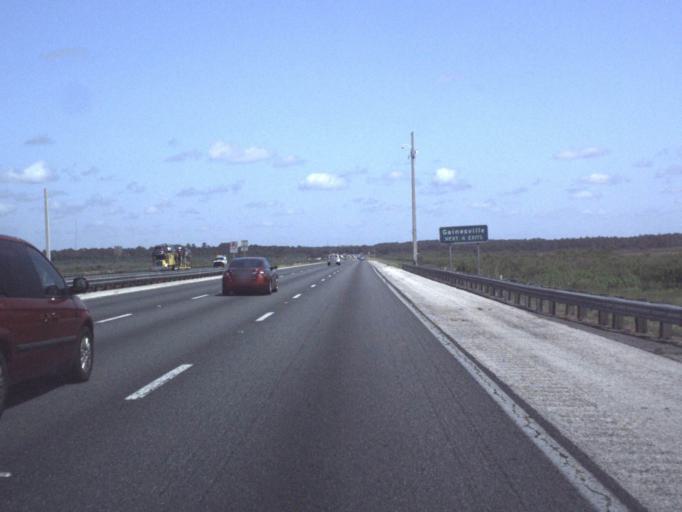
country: US
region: Florida
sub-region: Alachua County
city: Gainesville
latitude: 29.5722
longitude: -82.3522
